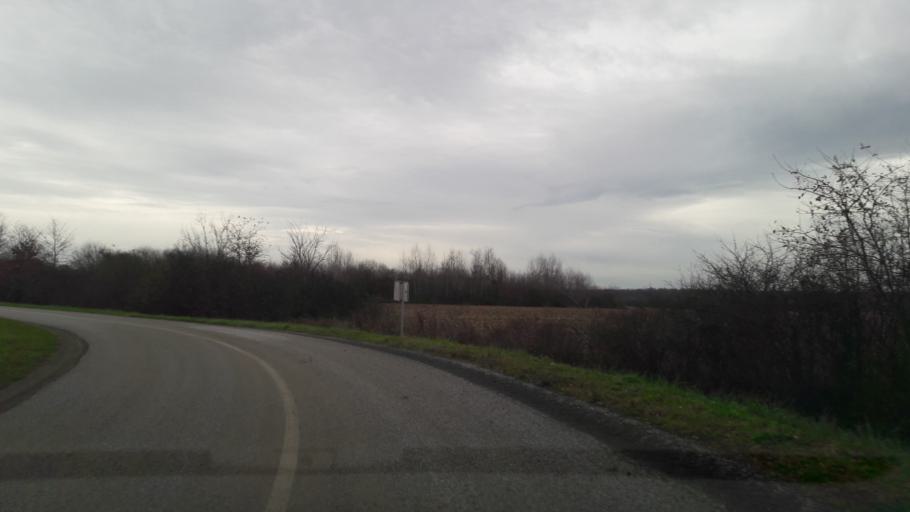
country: HR
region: Osjecko-Baranjska
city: Velimirovac
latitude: 45.6333
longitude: 18.1097
